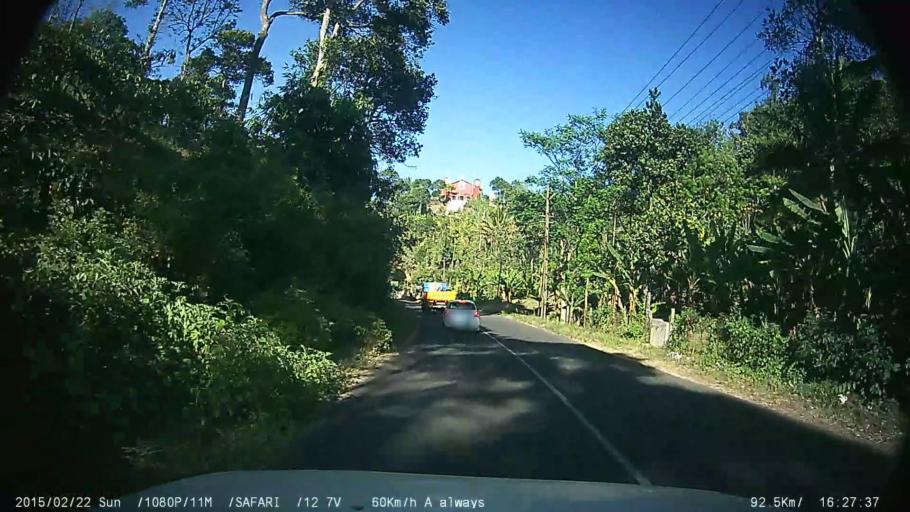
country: IN
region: Tamil Nadu
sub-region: Theni
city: Gudalur
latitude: 9.6054
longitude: 77.1432
